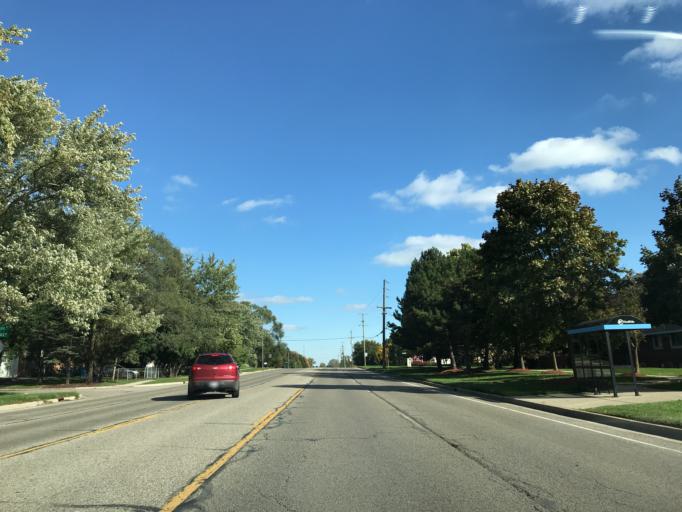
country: US
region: Michigan
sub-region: Washtenaw County
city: Ypsilanti
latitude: 42.2452
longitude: -83.6735
